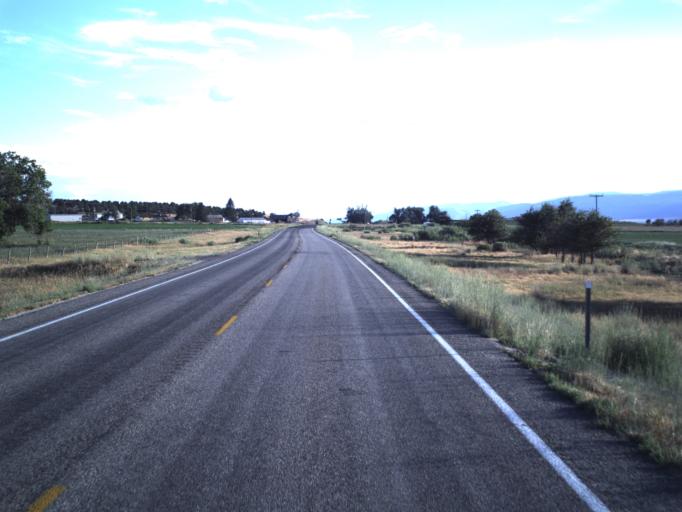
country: US
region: Utah
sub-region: Sanpete County
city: Moroni
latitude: 39.4859
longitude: -111.5178
